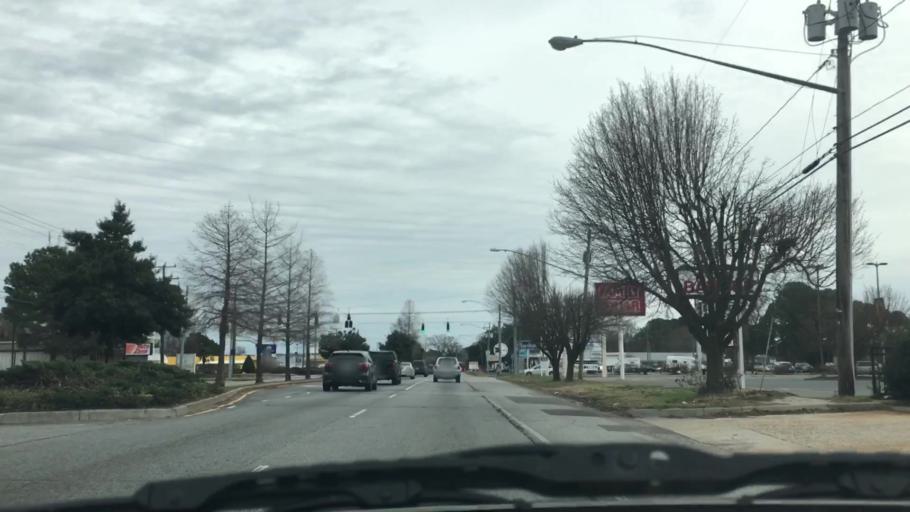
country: US
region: Virginia
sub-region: City of Norfolk
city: Norfolk
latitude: 36.9161
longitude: -76.2259
